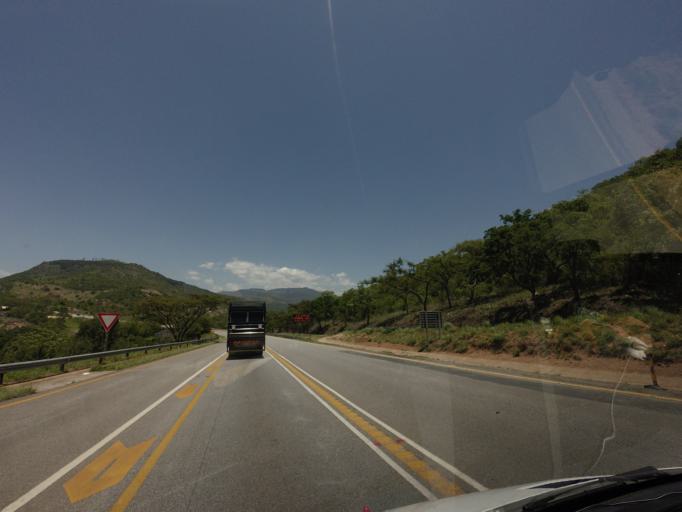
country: ZA
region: Mpumalanga
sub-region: Ehlanzeni District
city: Nelspruit
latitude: -25.4470
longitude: 30.7121
